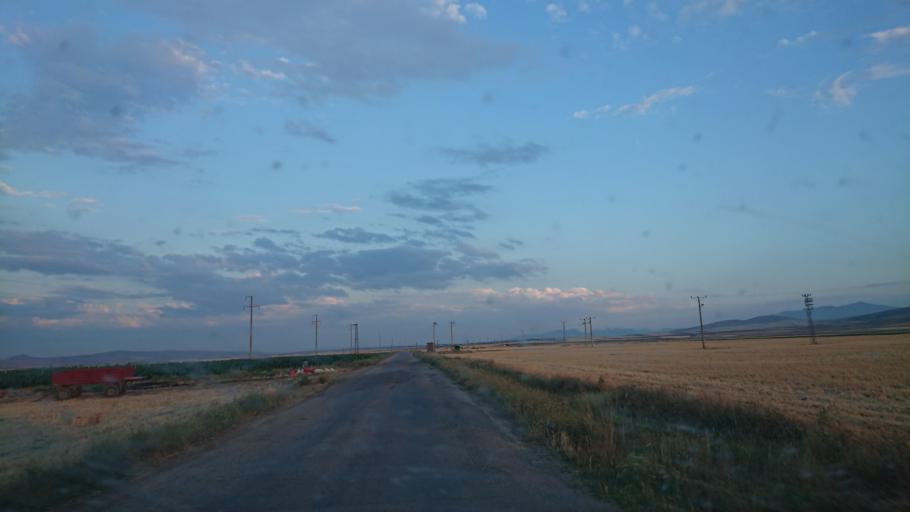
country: TR
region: Aksaray
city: Ortakoy
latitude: 38.8675
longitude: 34.0657
